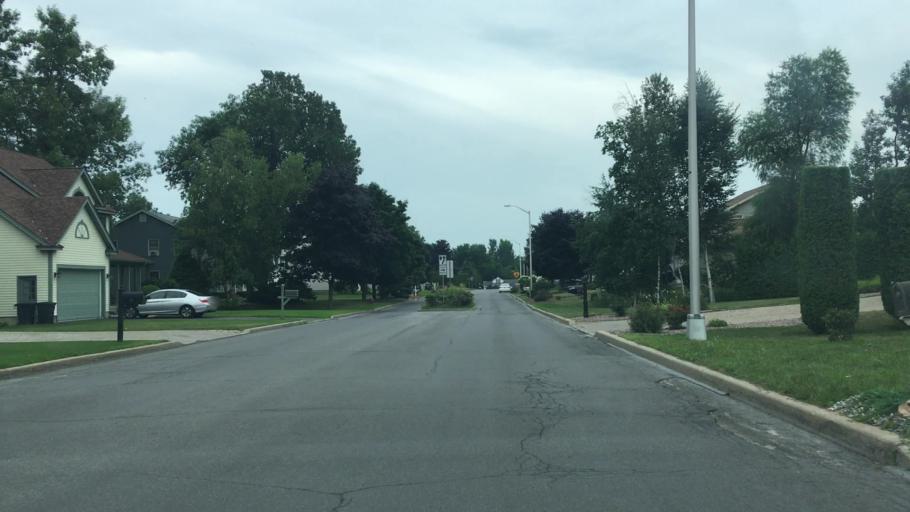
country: US
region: New York
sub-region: Clinton County
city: Plattsburgh West
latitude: 44.6906
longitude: -73.4826
